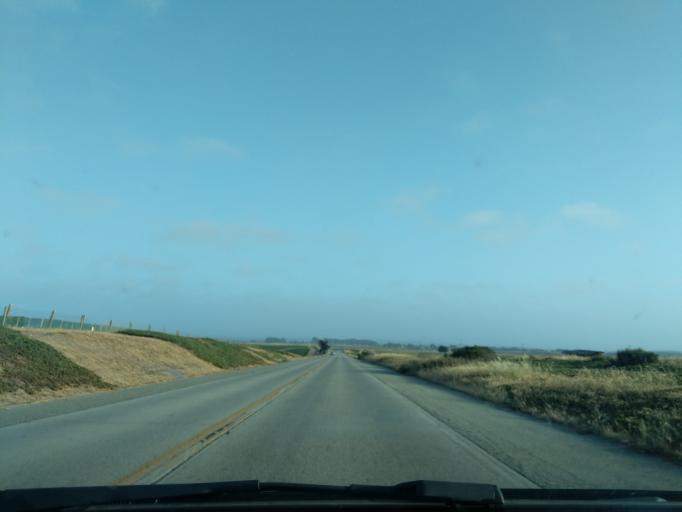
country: US
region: California
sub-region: Monterey County
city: Marina
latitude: 36.7133
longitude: -121.7882
